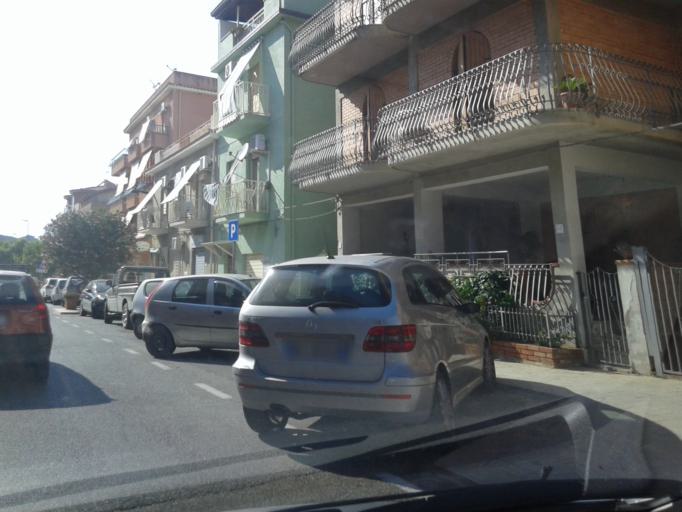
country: IT
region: Sicily
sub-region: Palermo
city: Finale
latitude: 38.0202
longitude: 14.1606
